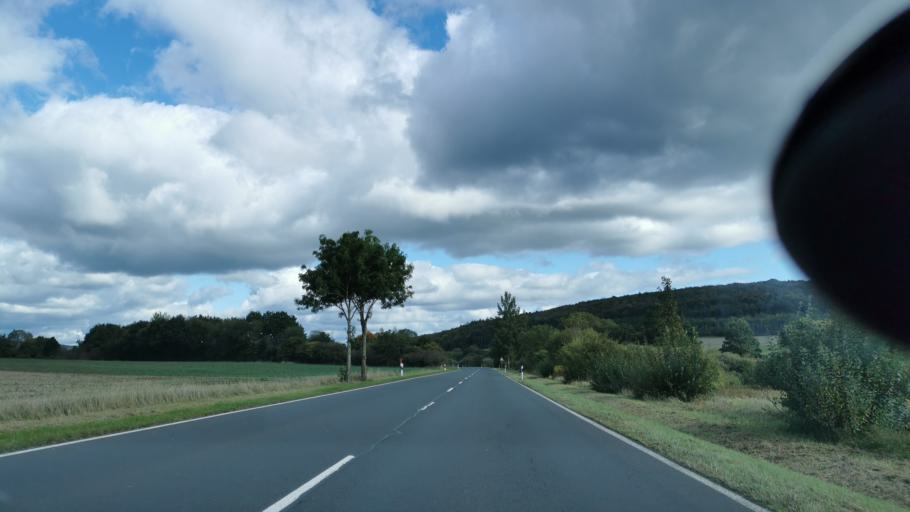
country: DE
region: Rheinland-Pfalz
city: Walsdorf
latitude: 50.2876
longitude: 6.7091
